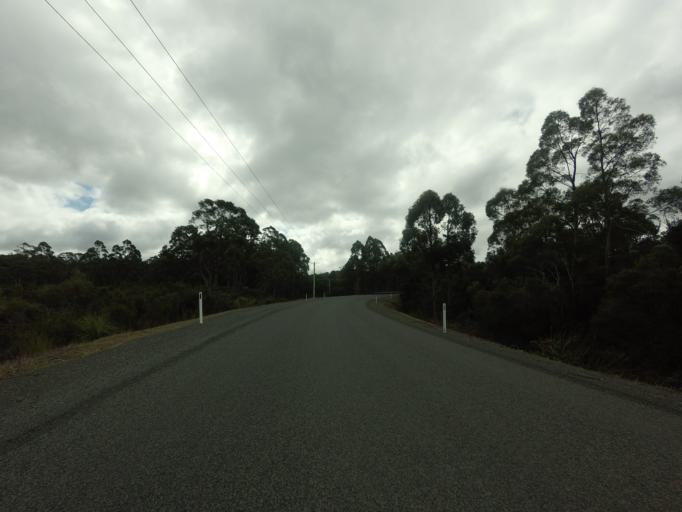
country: AU
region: Tasmania
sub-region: Huon Valley
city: Geeveston
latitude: -43.4220
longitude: 146.9050
